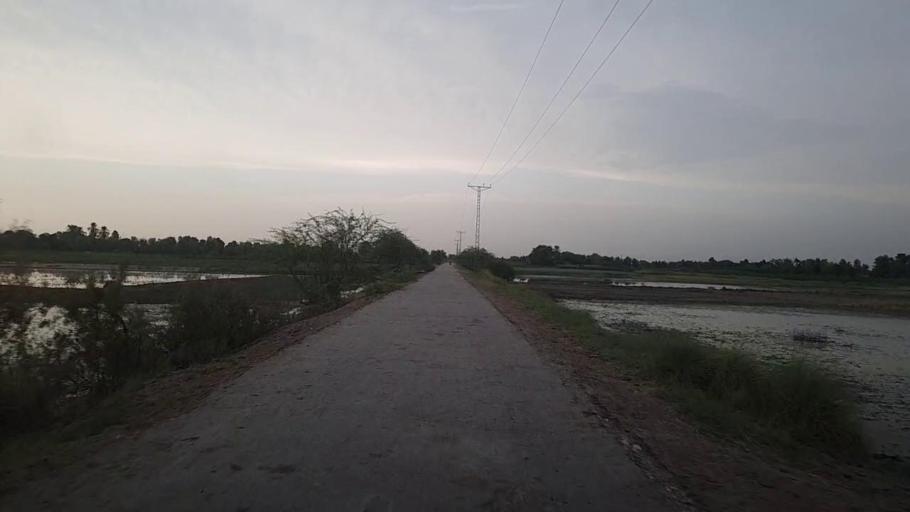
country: PK
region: Sindh
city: Karaundi
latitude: 27.0078
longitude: 68.3539
